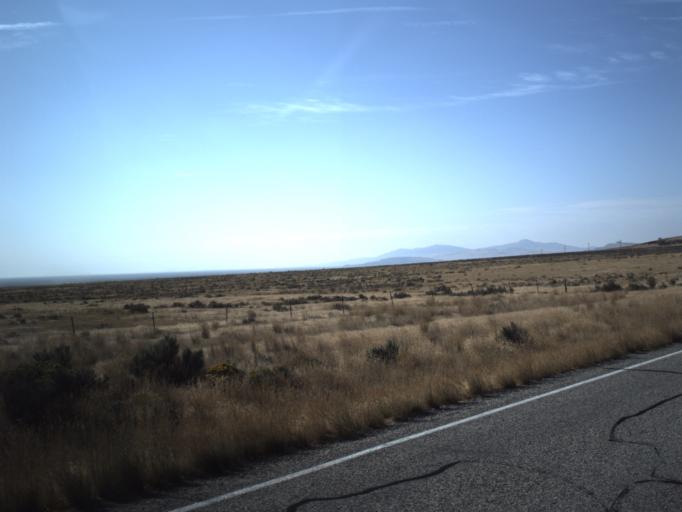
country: US
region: Idaho
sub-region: Minidoka County
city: Rupert
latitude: 41.8425
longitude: -113.1402
